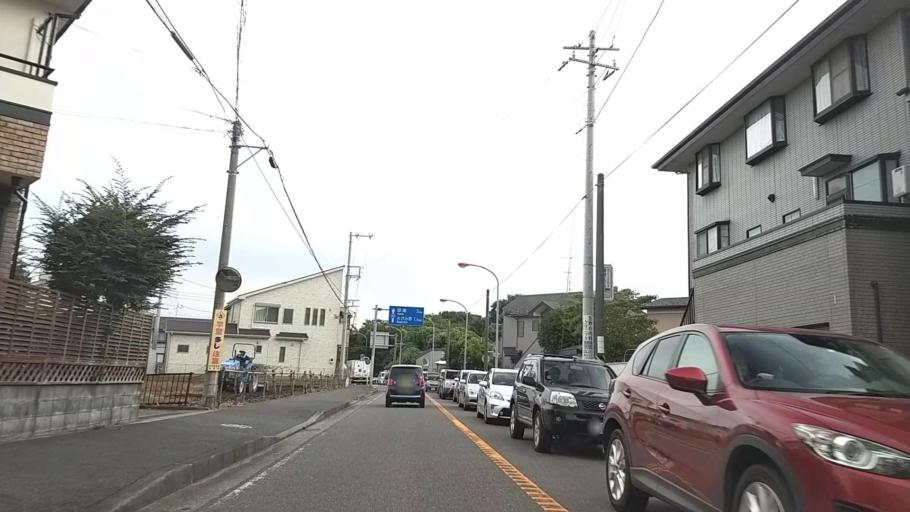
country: JP
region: Kanagawa
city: Zama
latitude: 35.4754
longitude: 139.4159
